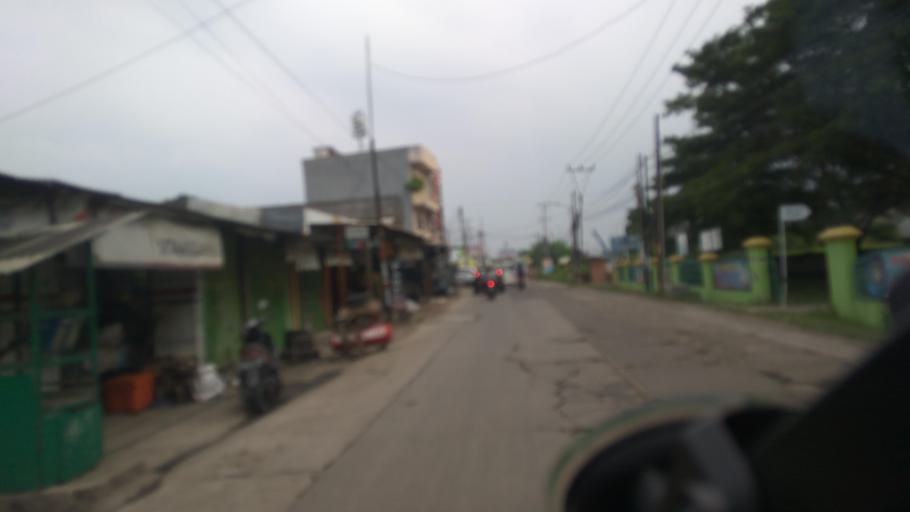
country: ID
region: West Java
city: Bekasi
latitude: -6.1992
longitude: 107.0380
